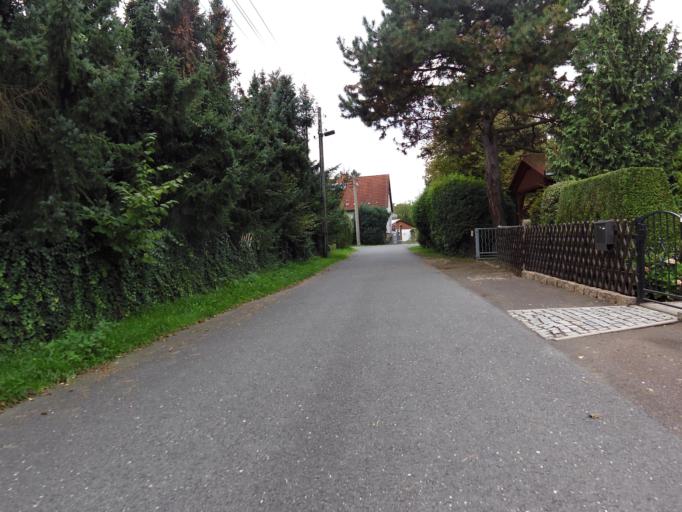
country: DE
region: Saxony
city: Grossposna
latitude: 51.3168
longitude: 12.4698
